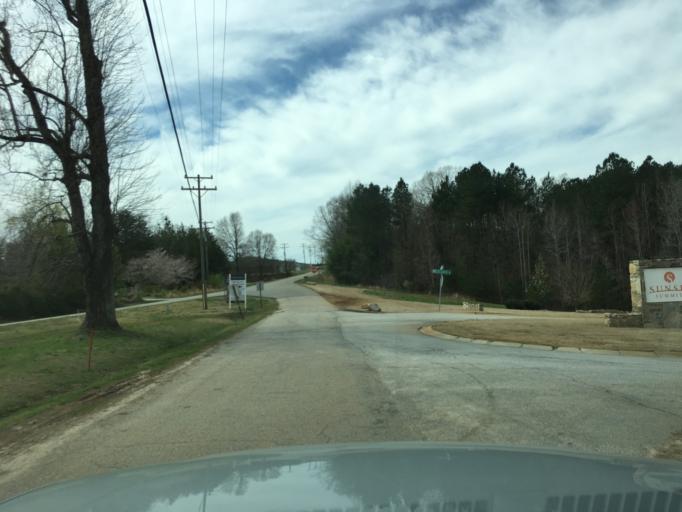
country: US
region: South Carolina
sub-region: Spartanburg County
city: Wellford
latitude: 34.8940
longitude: -82.0652
